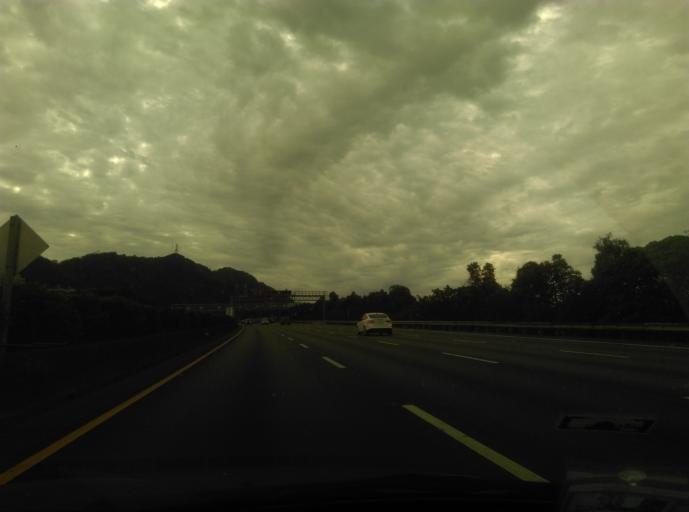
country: TW
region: Taiwan
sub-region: Taoyuan
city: Taoyuan
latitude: 24.9454
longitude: 121.3671
